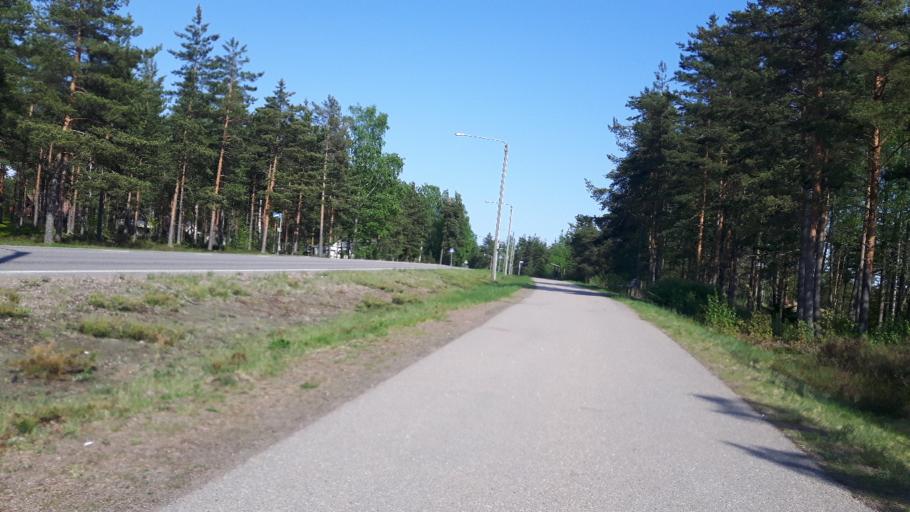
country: FI
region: Kymenlaakso
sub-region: Kotka-Hamina
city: Broby
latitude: 60.4875
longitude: 26.7523
